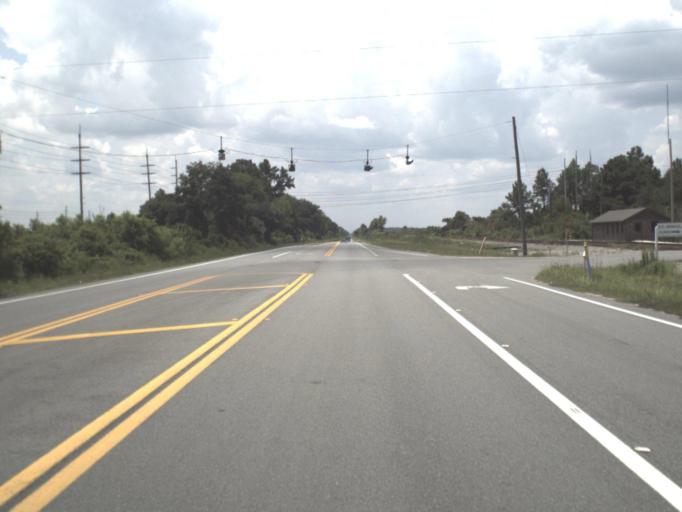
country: US
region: Florida
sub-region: Hamilton County
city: Jasper
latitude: 30.4358
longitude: -82.8714
